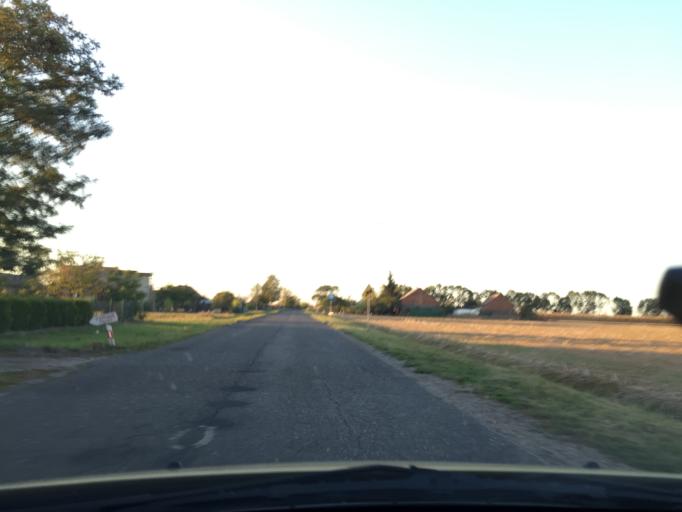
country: PL
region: Greater Poland Voivodeship
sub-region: Powiat pleszewski
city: Dobrzyca
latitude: 51.8276
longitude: 17.6200
